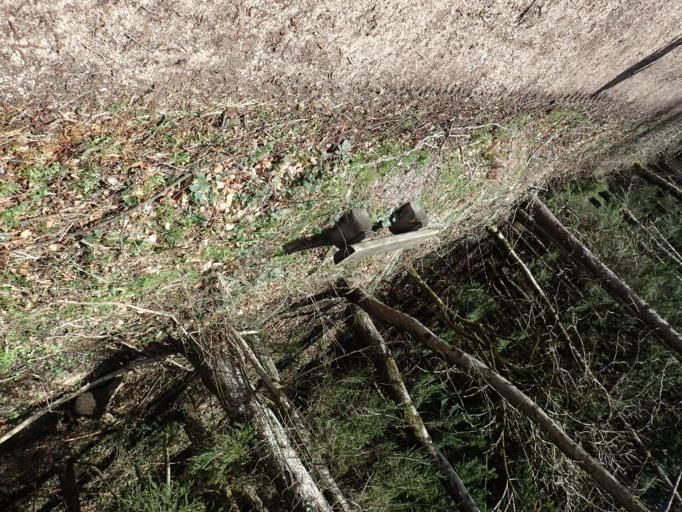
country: DE
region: Bavaria
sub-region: Upper Bavaria
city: Piding
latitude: 47.7943
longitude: 12.9173
